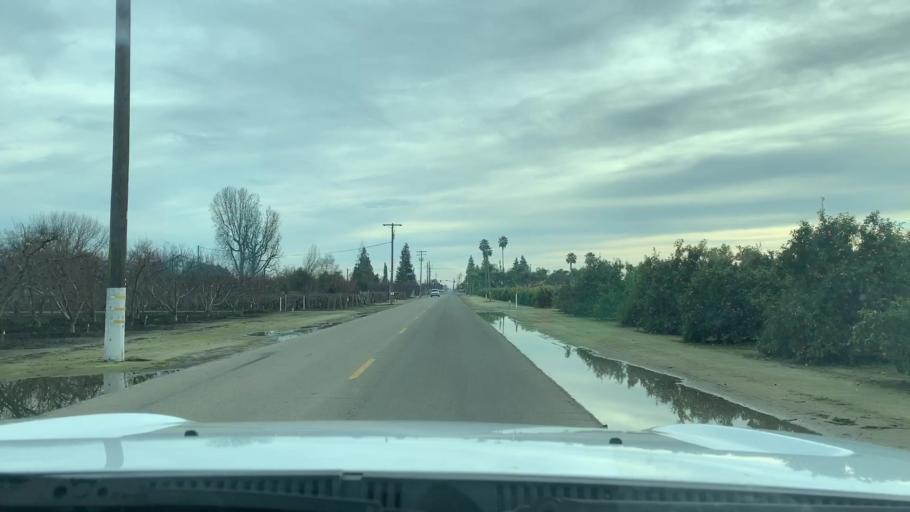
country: US
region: California
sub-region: Fresno County
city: Parlier
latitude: 36.6093
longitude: -119.5748
